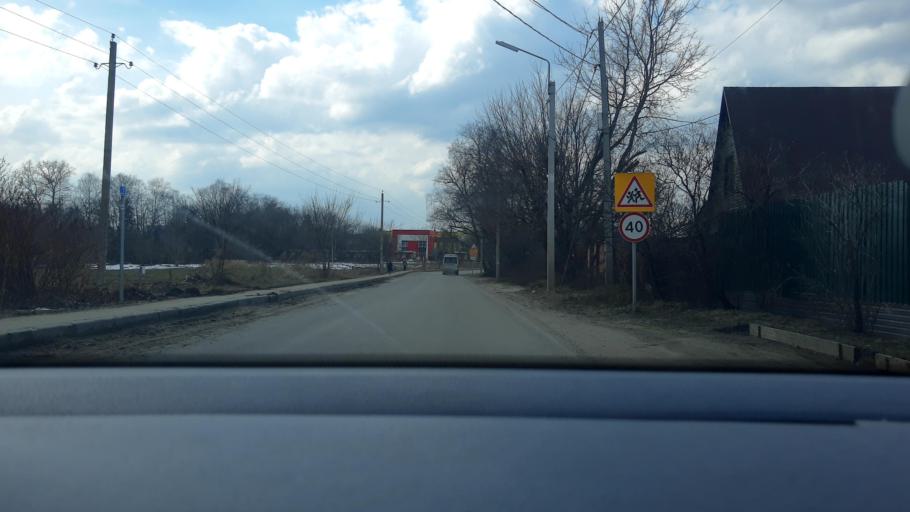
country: RU
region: Moskovskaya
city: Lesnyye Polyany
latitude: 55.9574
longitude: 37.8772
